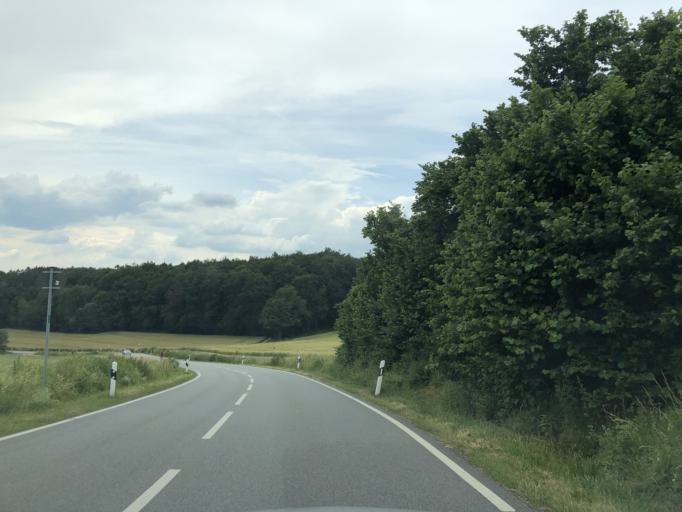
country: DE
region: Hesse
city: Lutzelbach
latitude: 49.7418
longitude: 8.7596
